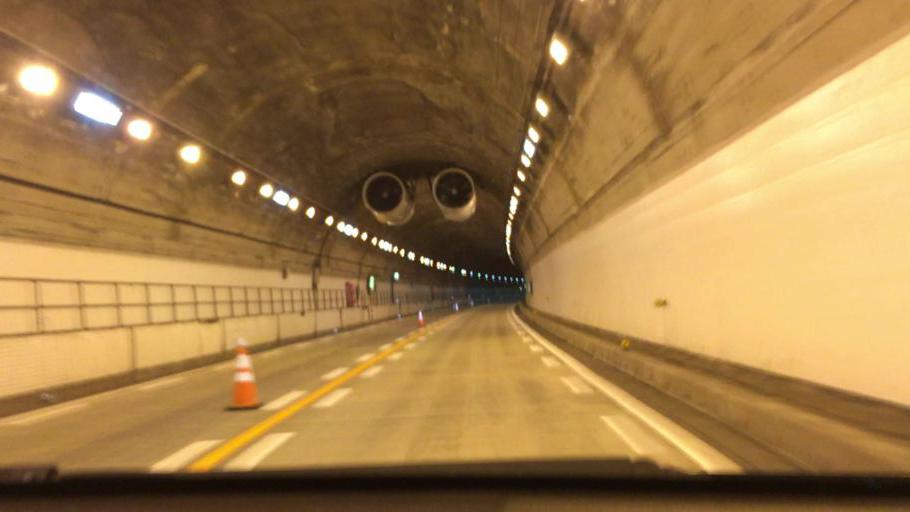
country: JP
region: Yamaguchi
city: Ogori-shimogo
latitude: 34.1015
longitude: 131.4506
